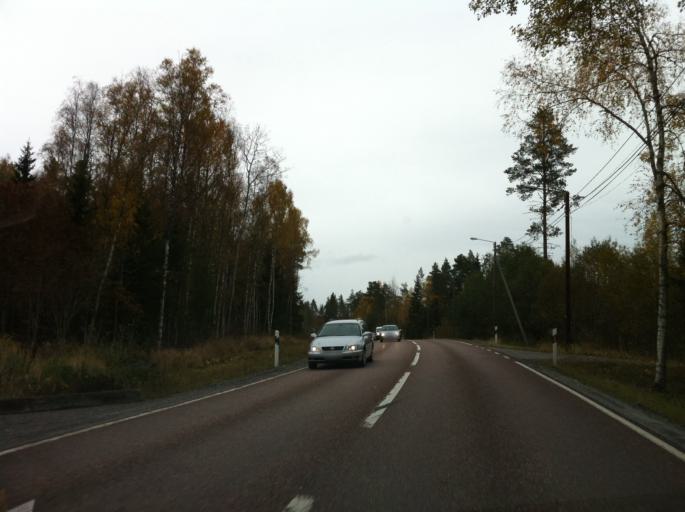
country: SE
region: Dalarna
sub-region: Ludvika Kommun
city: Grangesberg
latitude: 60.0377
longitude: 14.9681
